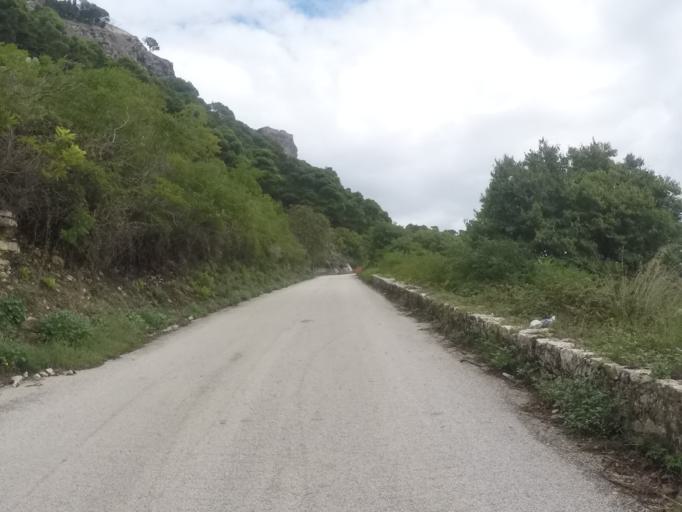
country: IT
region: Sicily
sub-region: Trapani
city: Erice
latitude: 38.0342
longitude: 12.5866
